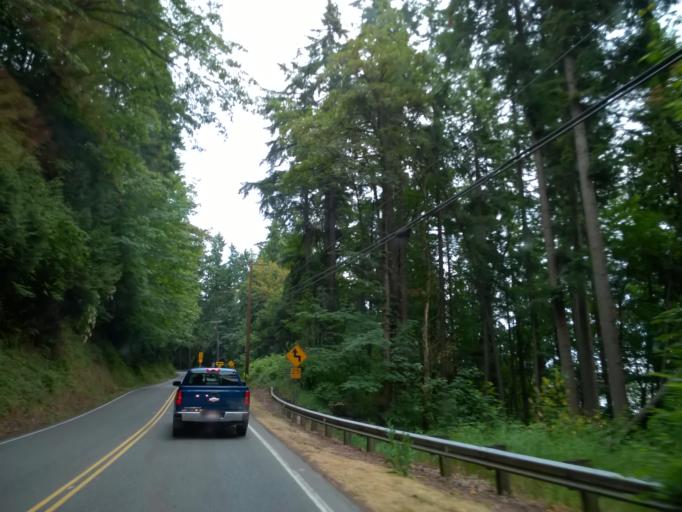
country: US
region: Washington
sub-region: King County
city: Sammamish
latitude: 47.6722
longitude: -122.0704
